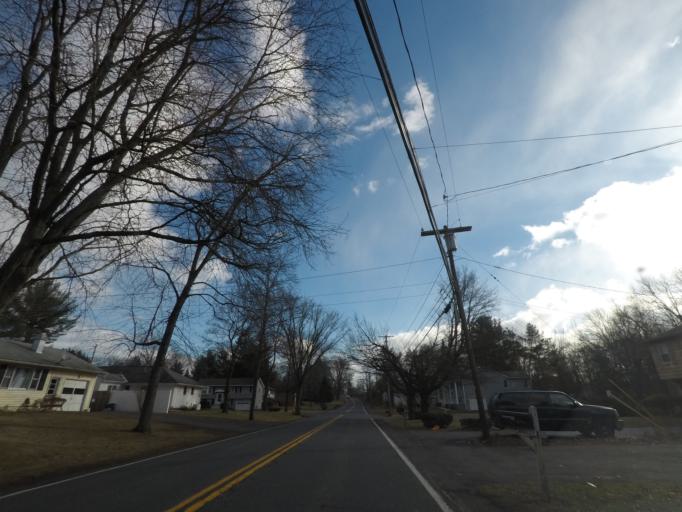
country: US
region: New York
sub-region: Schenectady County
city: Niskayuna
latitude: 42.7619
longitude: -73.8880
